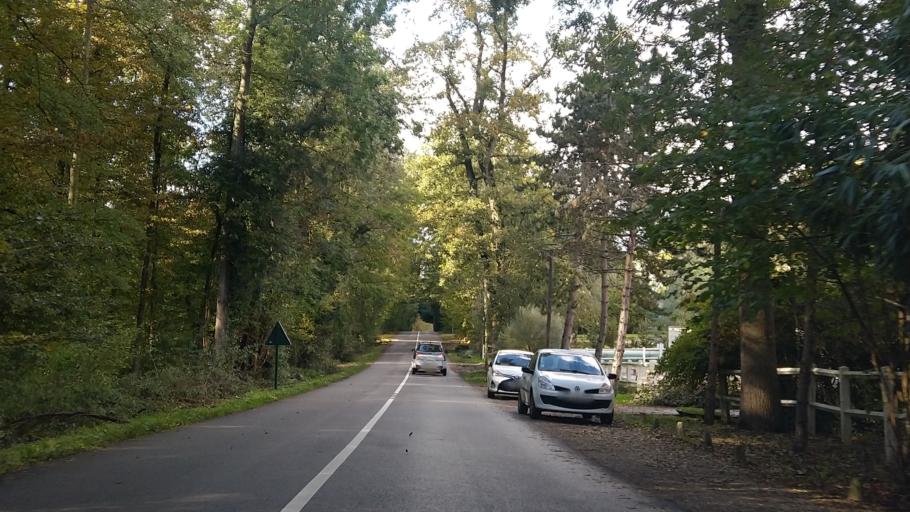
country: FR
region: Ile-de-France
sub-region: Departement du Val-d'Oise
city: Baillet-en-France
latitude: 49.0748
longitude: 2.2782
